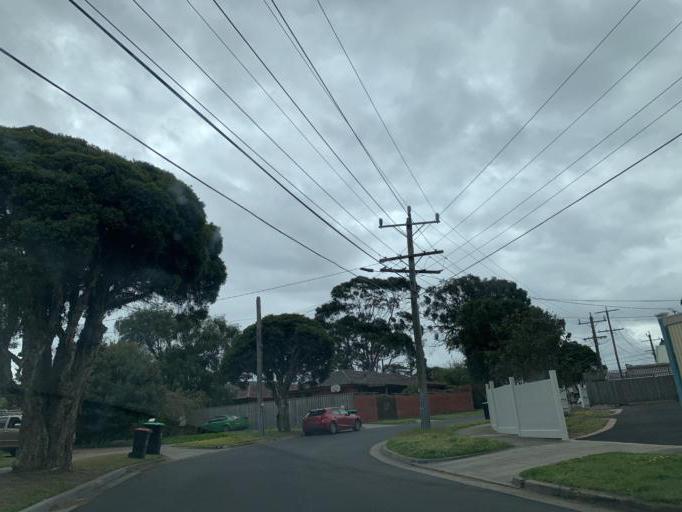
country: AU
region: Victoria
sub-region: Kingston
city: Mentone
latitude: -37.9689
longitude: 145.0772
